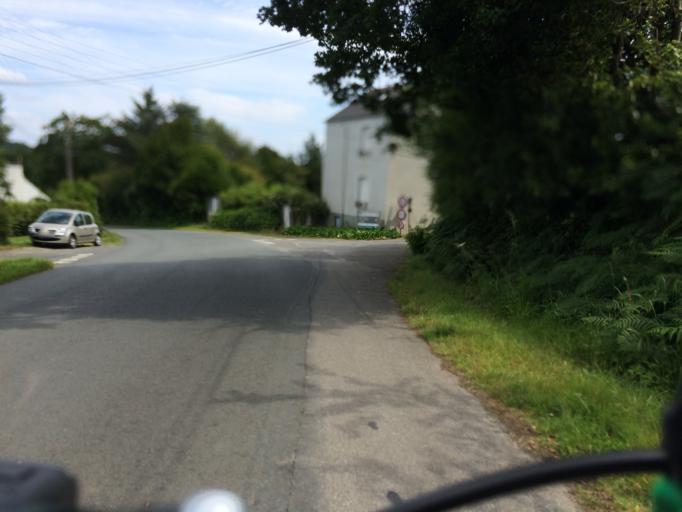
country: FR
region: Brittany
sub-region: Departement du Finistere
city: Logonna-Daoulas
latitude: 48.3189
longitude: -4.2945
